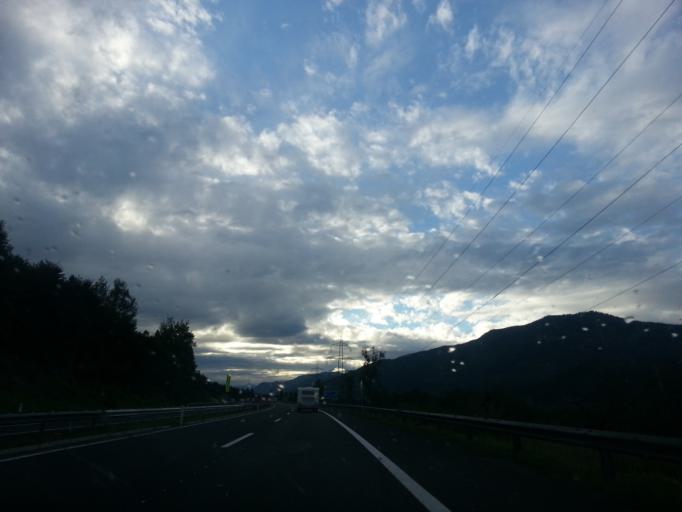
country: AT
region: Styria
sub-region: Politischer Bezirk Liezen
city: Treglwang
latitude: 47.4778
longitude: 14.5686
